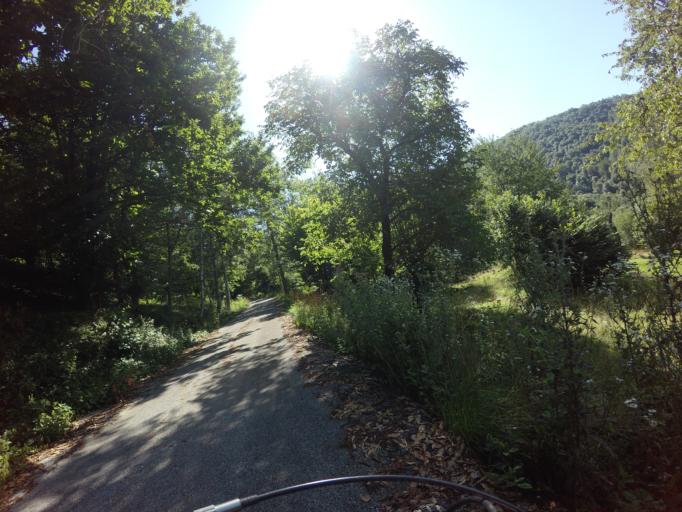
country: IT
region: Piedmont
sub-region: Provincia di Cuneo
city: Chiusa di Pesio
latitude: 44.2821
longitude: 7.6777
